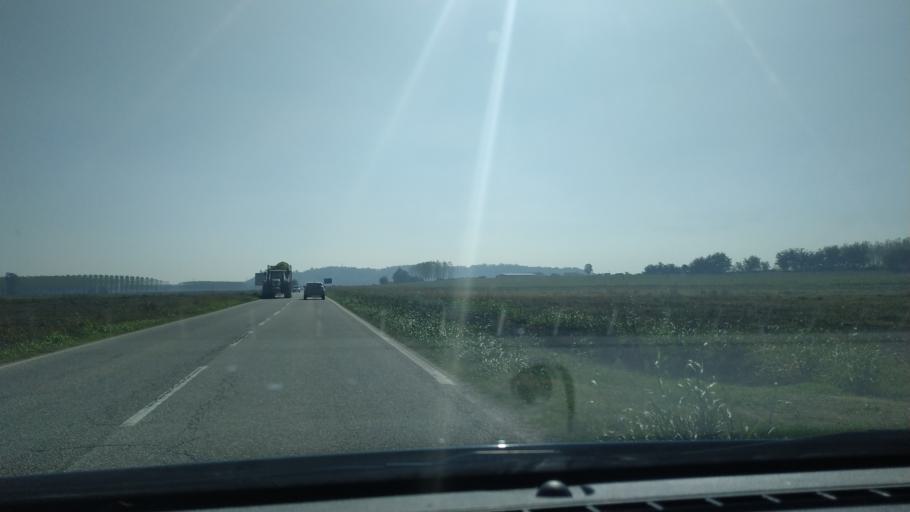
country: IT
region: Piedmont
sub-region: Provincia di Alessandria
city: Giarole
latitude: 45.0769
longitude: 8.5701
